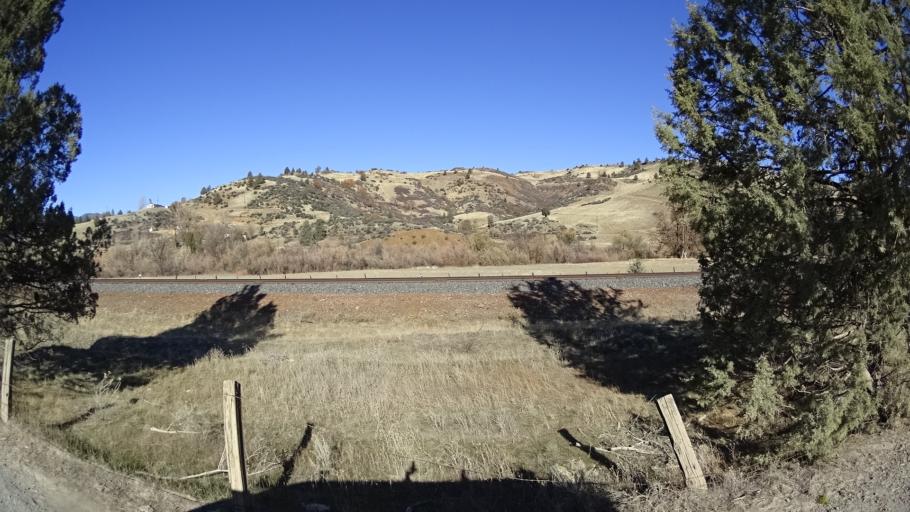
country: US
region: California
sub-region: Siskiyou County
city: Montague
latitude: 41.8975
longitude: -122.5158
